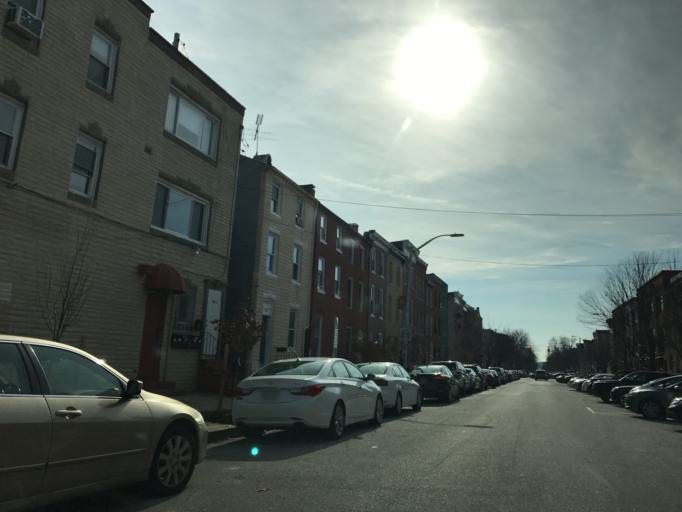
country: US
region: Maryland
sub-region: City of Baltimore
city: Baltimore
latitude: 39.2904
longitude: -76.5917
